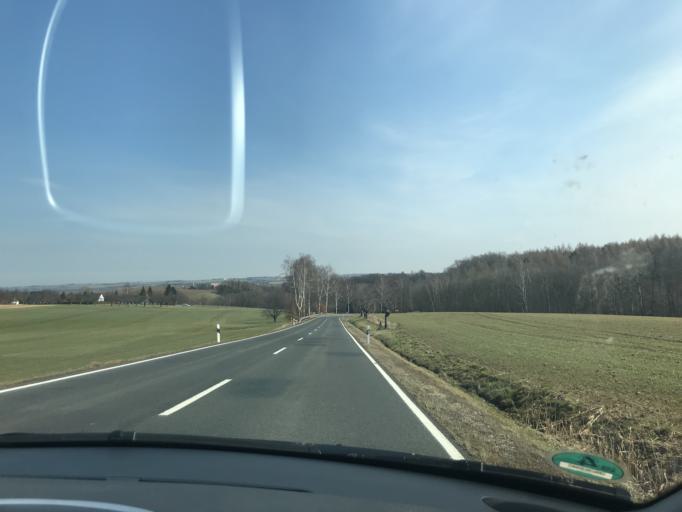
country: DE
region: Saxony
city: Rochlitz
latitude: 51.0353
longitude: 12.7657
